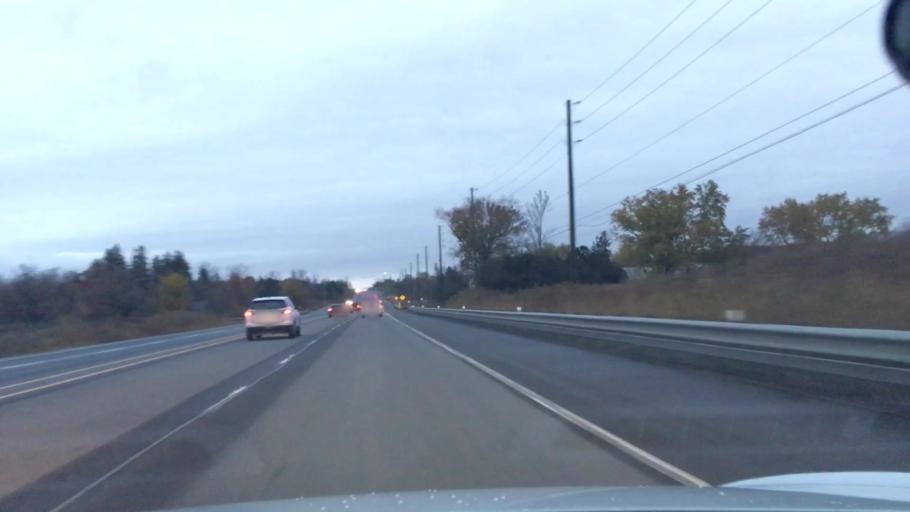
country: CA
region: Ontario
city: Ajax
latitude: 43.9344
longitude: -79.0414
